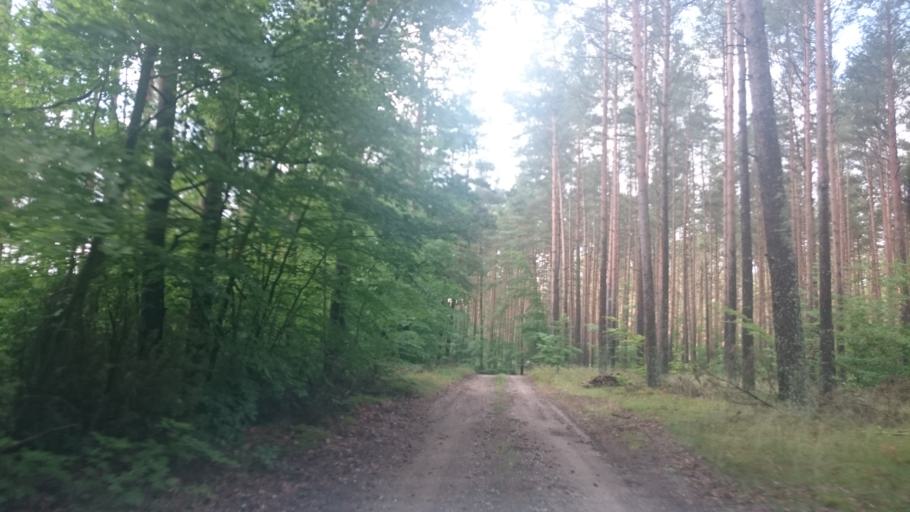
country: PL
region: Pomeranian Voivodeship
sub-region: Powiat koscierski
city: Karsin
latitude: 54.0017
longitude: 17.9309
